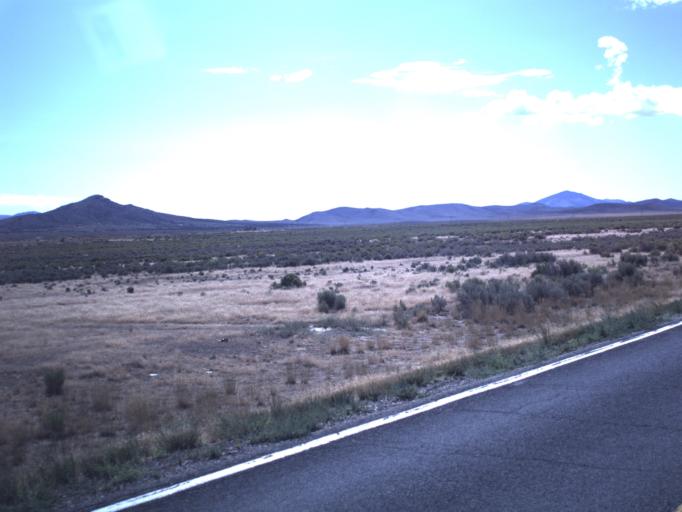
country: US
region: Utah
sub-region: Tooele County
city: Tooele
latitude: 40.1276
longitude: -112.4308
